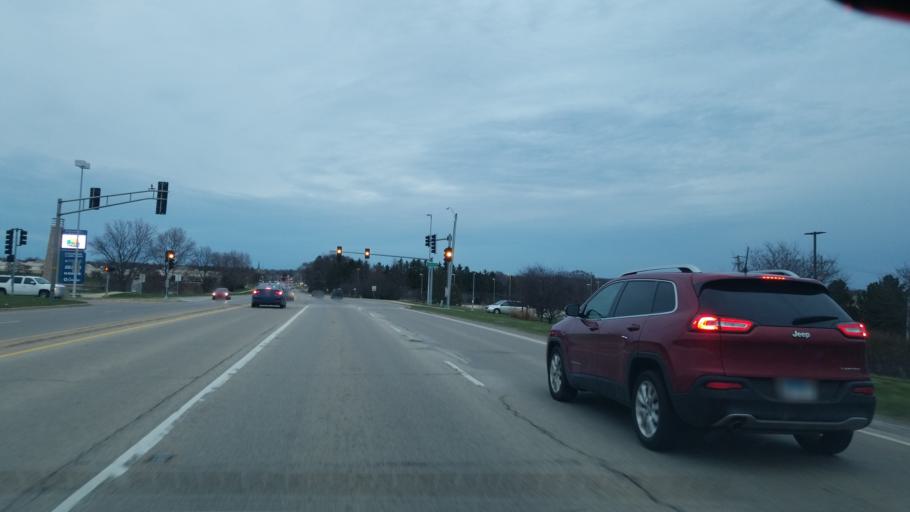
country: US
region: Illinois
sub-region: Kane County
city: Sleepy Hollow
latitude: 42.0993
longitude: -88.2978
